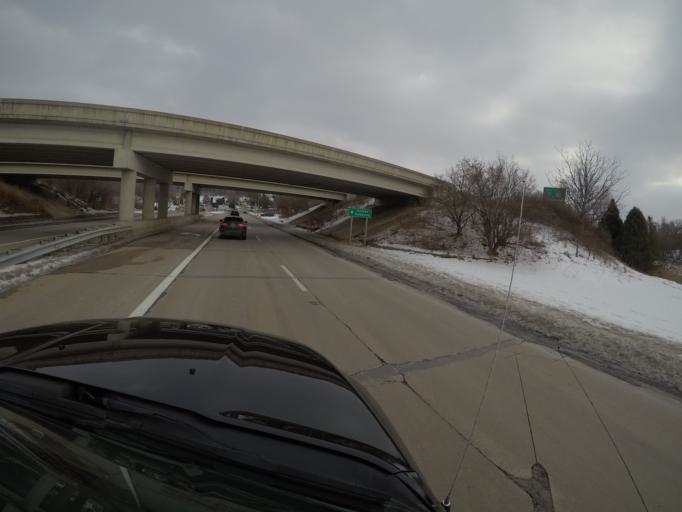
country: US
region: Wisconsin
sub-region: La Crosse County
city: Onalaska
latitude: 43.8842
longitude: -91.2119
